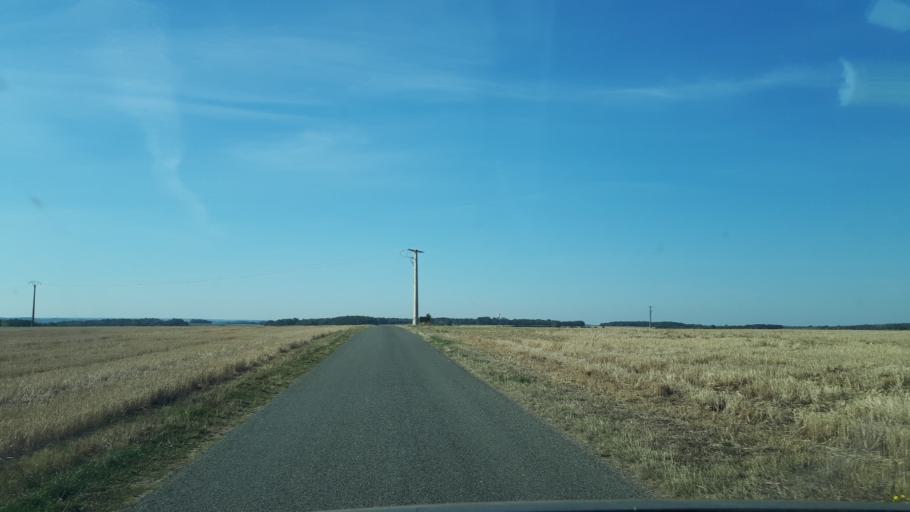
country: FR
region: Centre
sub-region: Departement du Loir-et-Cher
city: Lunay
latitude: 47.8334
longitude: 0.9515
